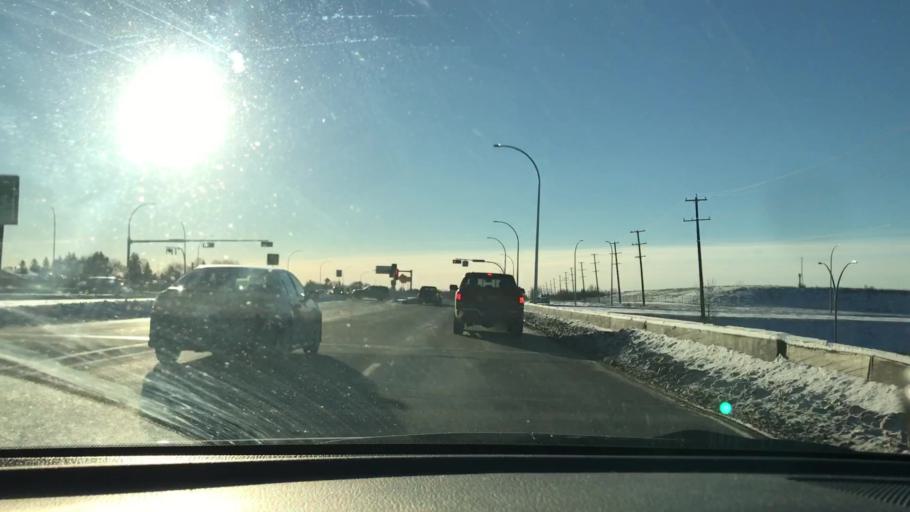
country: CA
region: Alberta
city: Edmonton
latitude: 53.4834
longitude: -113.4671
